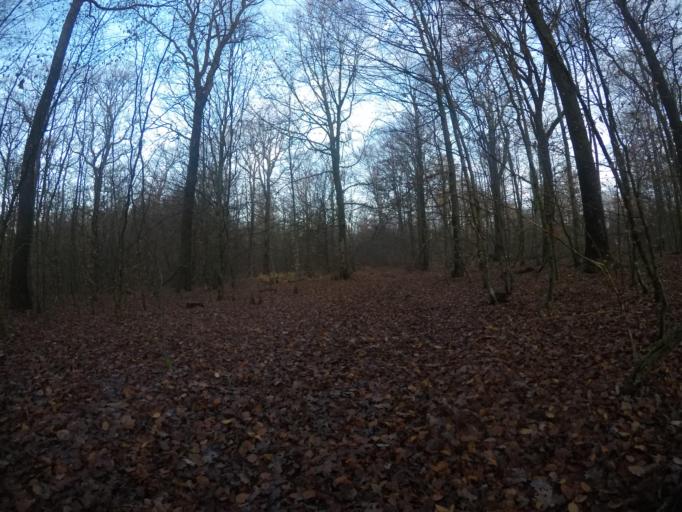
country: BE
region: Wallonia
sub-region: Province du Luxembourg
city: Habay-la-Vieille
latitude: 49.7465
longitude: 5.6727
